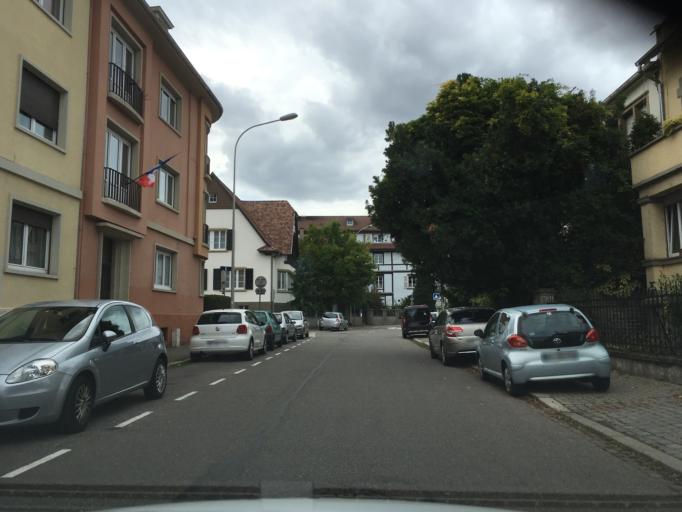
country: FR
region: Alsace
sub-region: Departement du Bas-Rhin
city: Strasbourg
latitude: 48.5631
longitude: 7.7586
